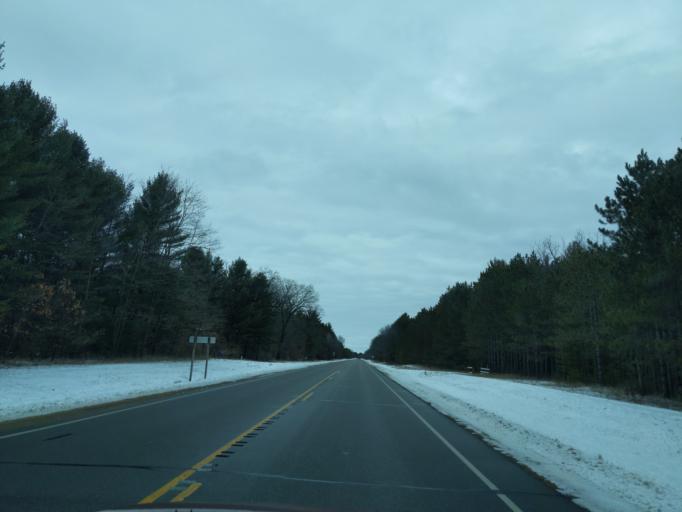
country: US
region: Wisconsin
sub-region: Marquette County
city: Montello
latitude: 43.9208
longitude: -89.3122
